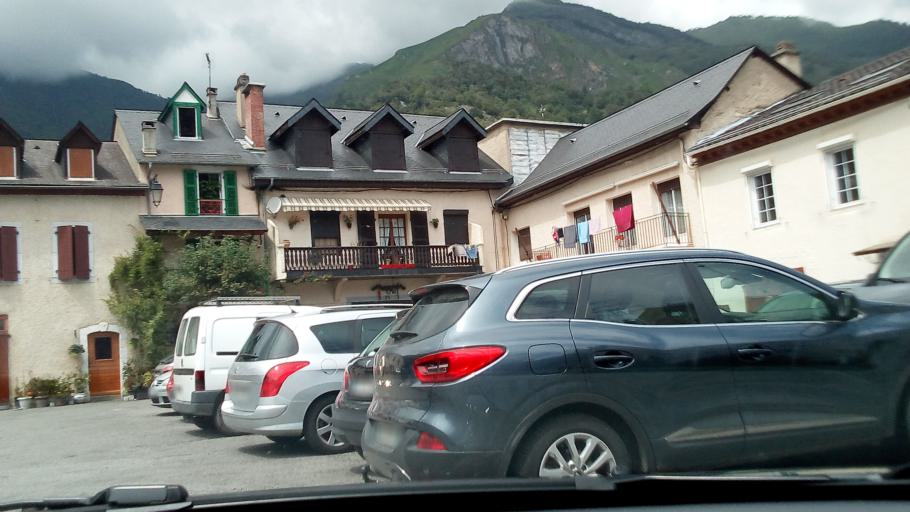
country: FR
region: Aquitaine
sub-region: Departement des Pyrenees-Atlantiques
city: Laruns
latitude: 42.9859
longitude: -0.4274
